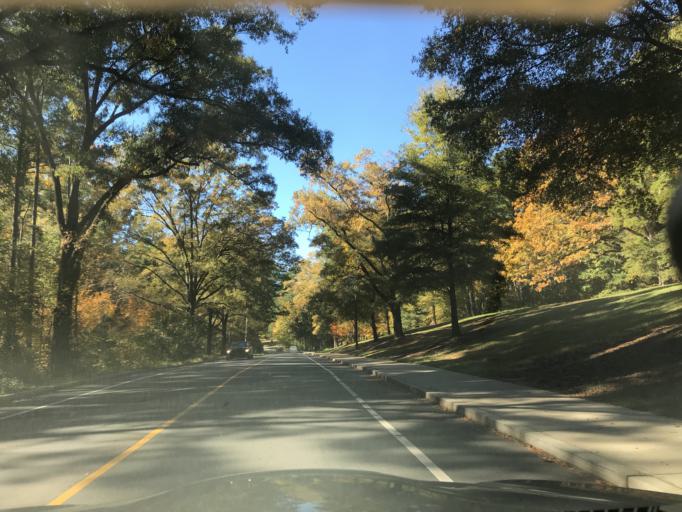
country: US
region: North Carolina
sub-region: Durham County
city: Durham
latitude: 36.0000
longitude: -78.9235
